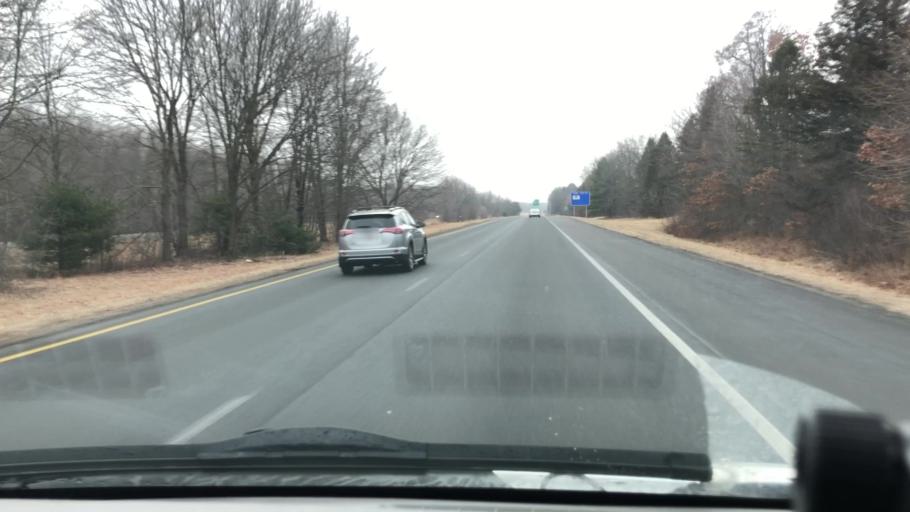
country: US
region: Massachusetts
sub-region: Hampshire County
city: Hatfield
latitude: 42.3809
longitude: -72.6319
